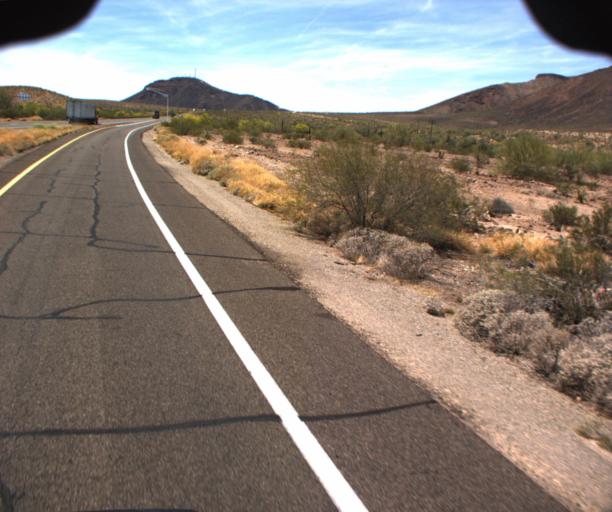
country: US
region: Arizona
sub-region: La Paz County
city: Quartzsite
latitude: 33.6629
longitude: -114.0164
